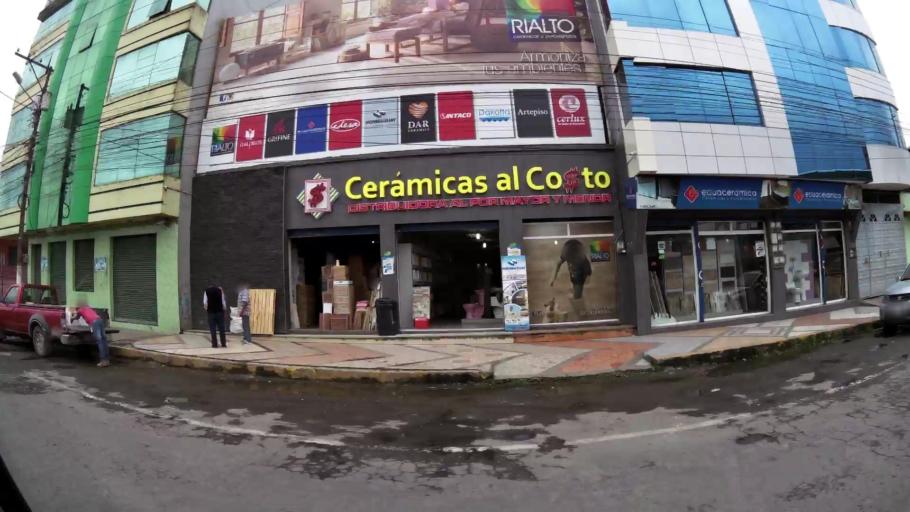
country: EC
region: Santo Domingo de los Tsachilas
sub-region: Canton Santo Domingo de los Colorados
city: Santo Domingo de los Colorados
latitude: -0.2441
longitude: -79.1683
